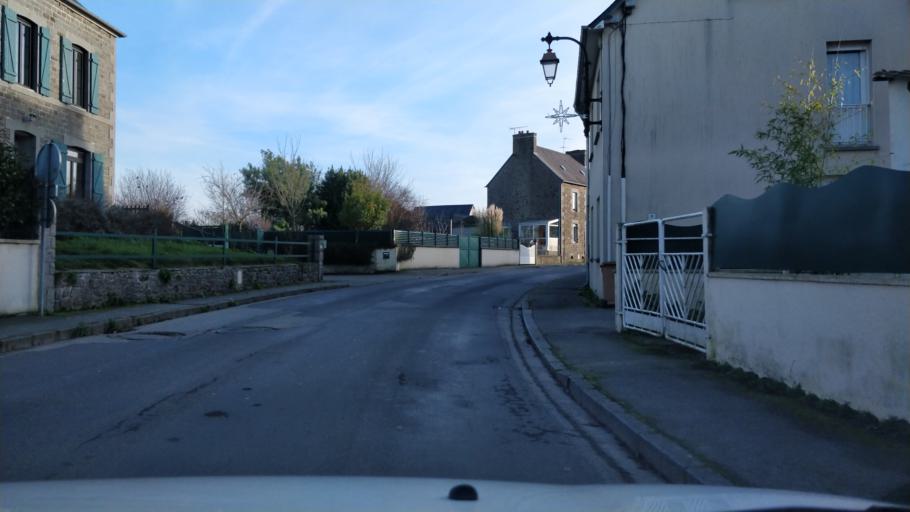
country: FR
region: Brittany
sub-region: Departement d'Ille-et-Vilaine
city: Plerguer
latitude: 48.5260
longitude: -1.8478
